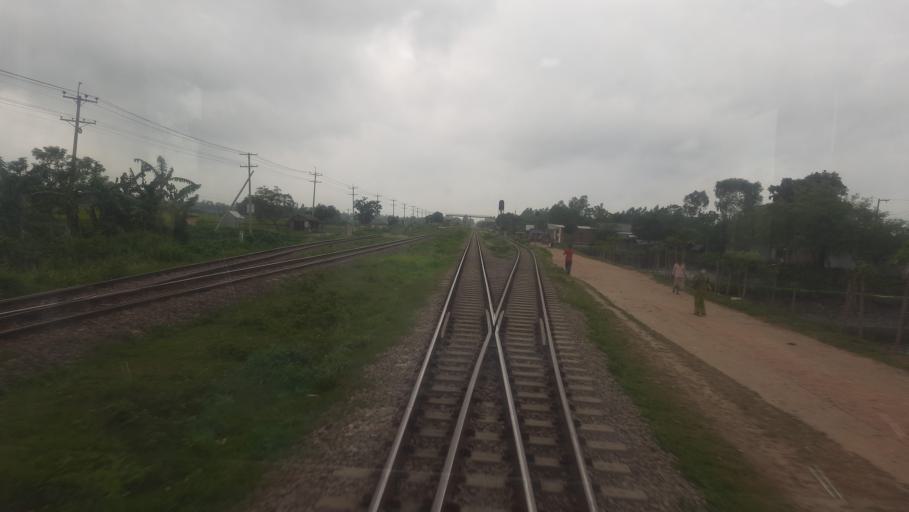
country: BD
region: Dhaka
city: Narsingdi
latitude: 23.9555
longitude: 90.8015
